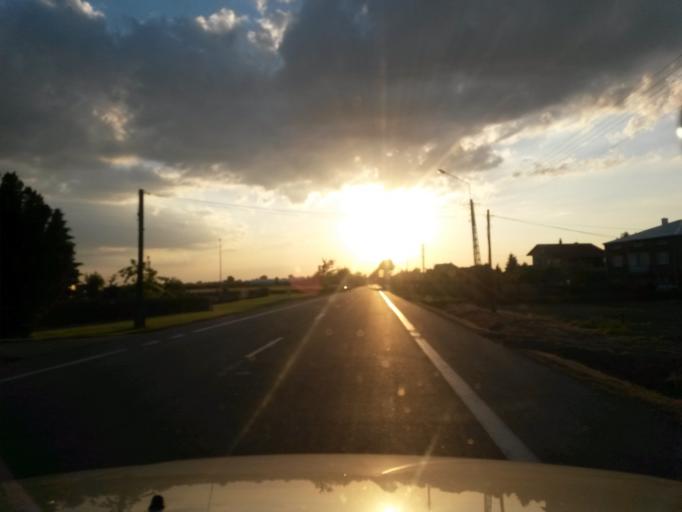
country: PL
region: Lodz Voivodeship
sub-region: Powiat wielunski
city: Czarnozyly
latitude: 51.2570
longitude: 18.4924
